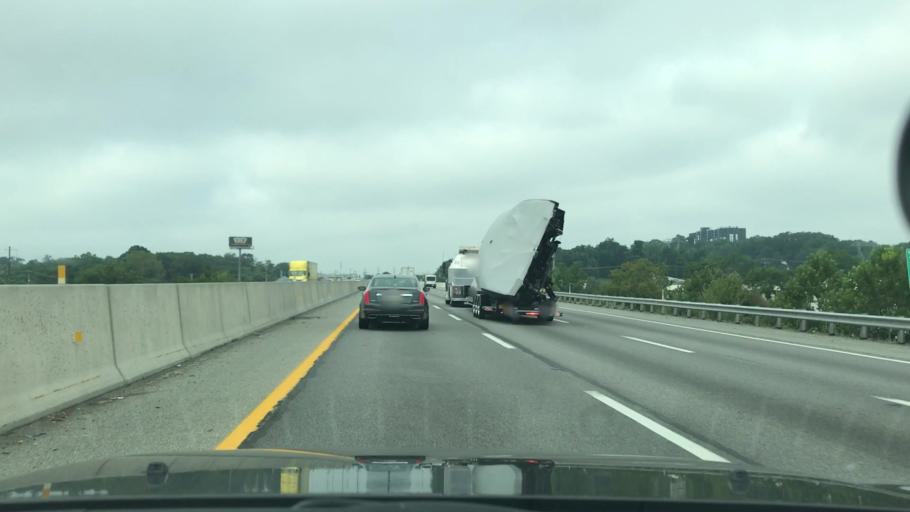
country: US
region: Pennsylvania
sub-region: Montgomery County
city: Bridgeport
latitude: 40.0882
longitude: -75.3542
